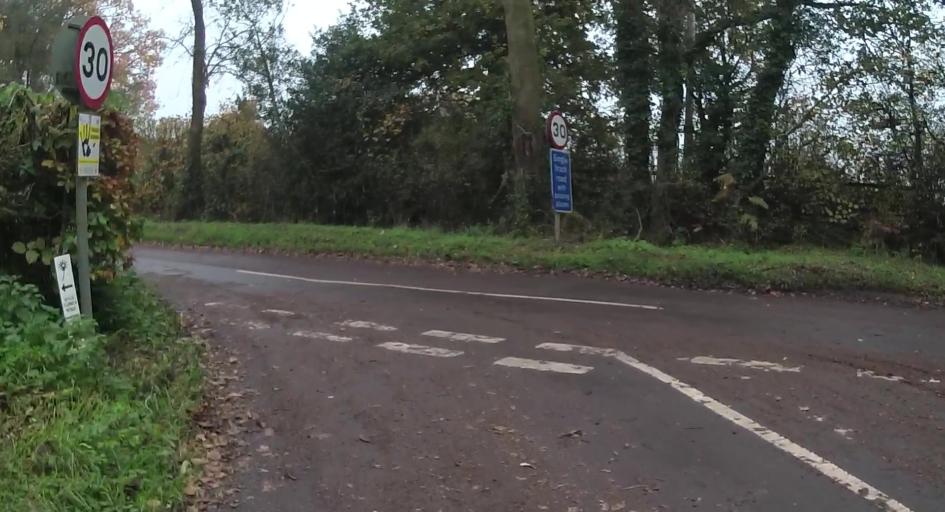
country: GB
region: England
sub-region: Hampshire
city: Old Basing
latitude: 51.2046
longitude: -1.0390
